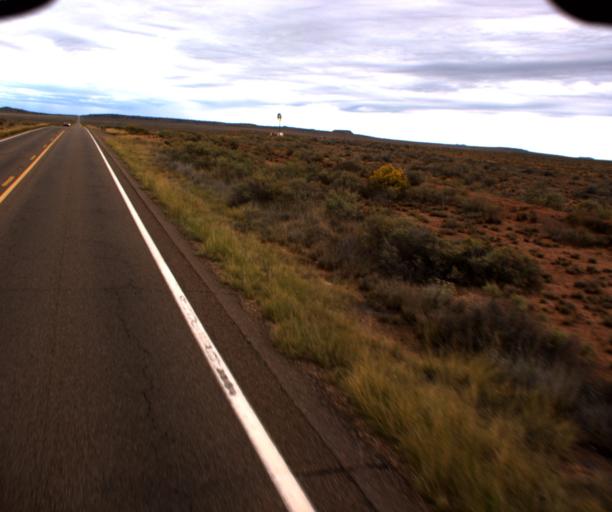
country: US
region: Arizona
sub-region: Navajo County
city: Holbrook
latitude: 34.7369
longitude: -110.1184
